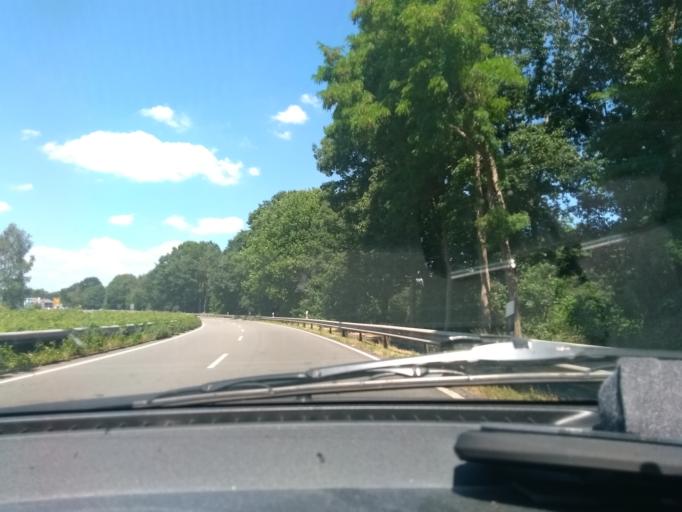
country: DE
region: Lower Saxony
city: Meppen
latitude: 52.6795
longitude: 7.3037
